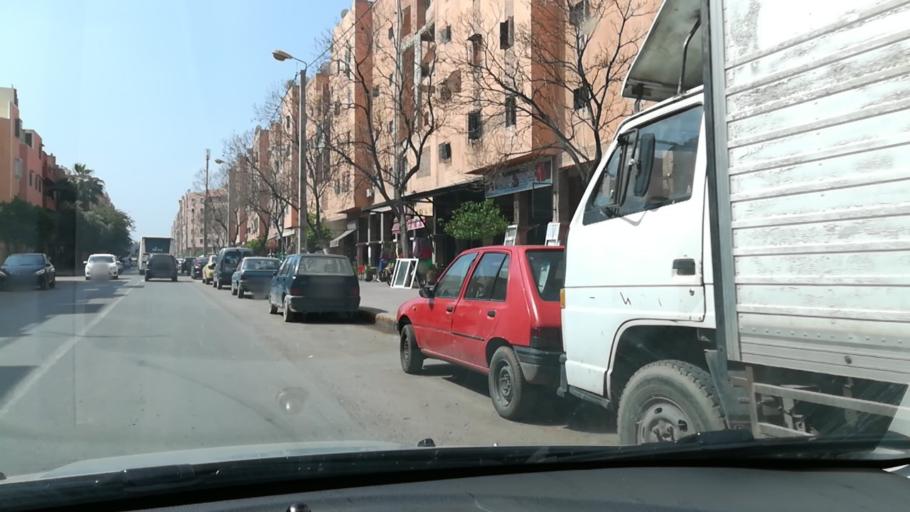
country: MA
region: Marrakech-Tensift-Al Haouz
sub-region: Marrakech
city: Marrakesh
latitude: 31.6331
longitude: -8.0624
